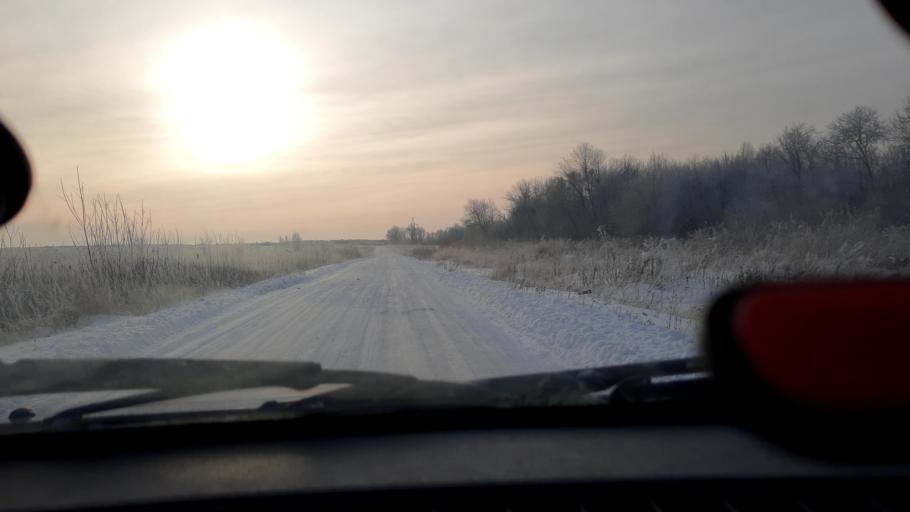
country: RU
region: Bashkortostan
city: Iglino
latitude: 54.7375
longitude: 56.2425
